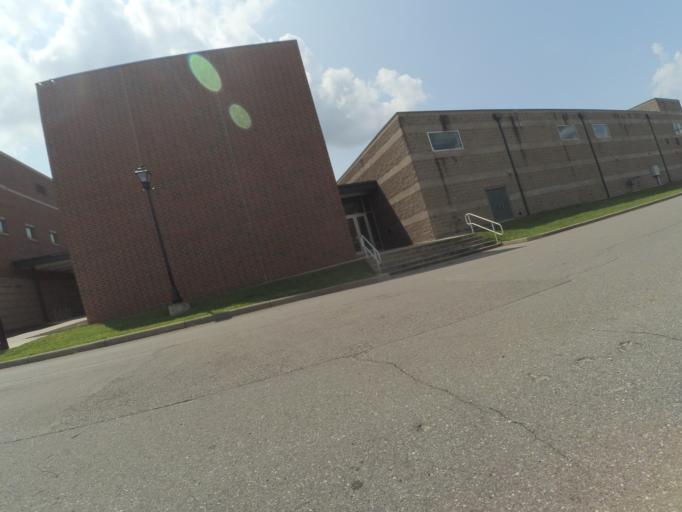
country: US
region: West Virginia
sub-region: Cabell County
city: Huntington
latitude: 38.4249
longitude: -82.4305
